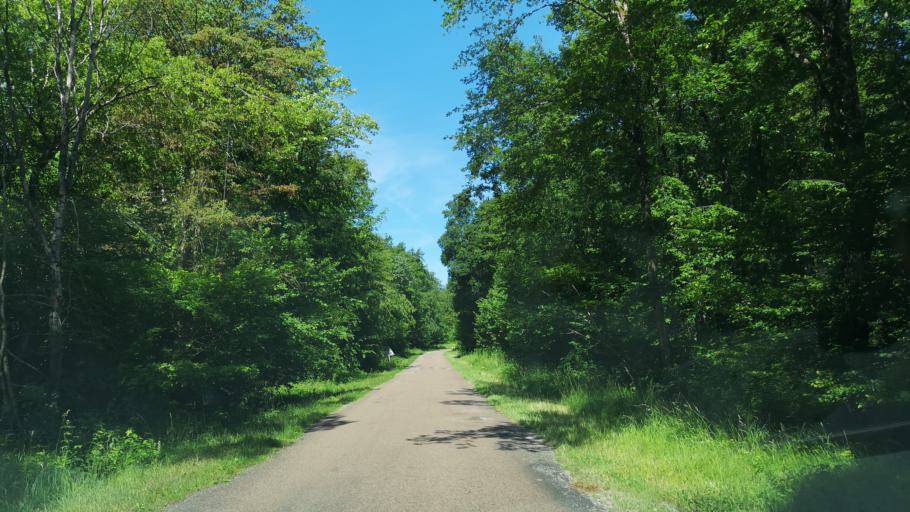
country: FR
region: Lorraine
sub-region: Departement de la Meuse
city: Vigneulles-les-Hattonchatel
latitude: 49.0280
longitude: 5.6454
